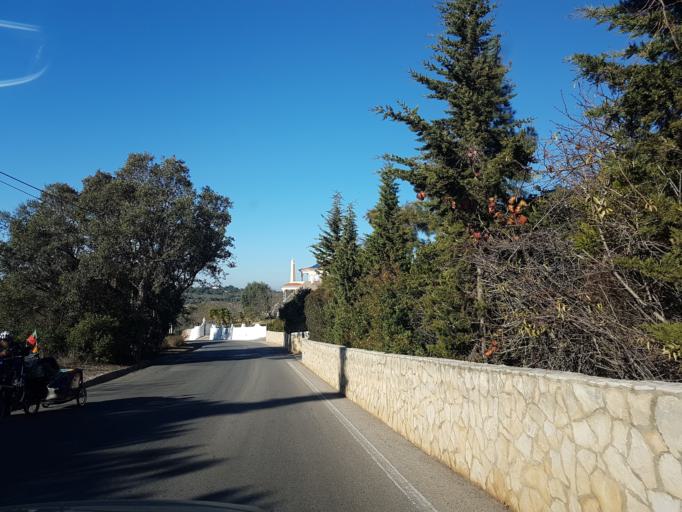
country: PT
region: Faro
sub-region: Silves
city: Armacao de Pera
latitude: 37.1162
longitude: -8.4056
